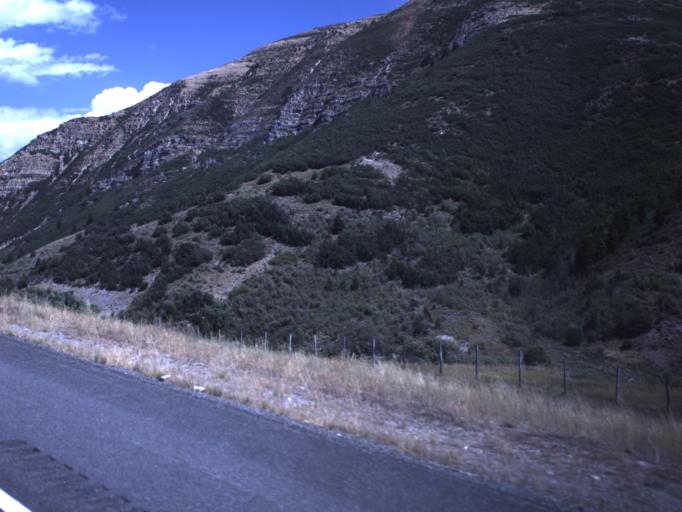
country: US
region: Utah
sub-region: Wasatch County
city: Midway
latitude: 40.3928
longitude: -111.5419
